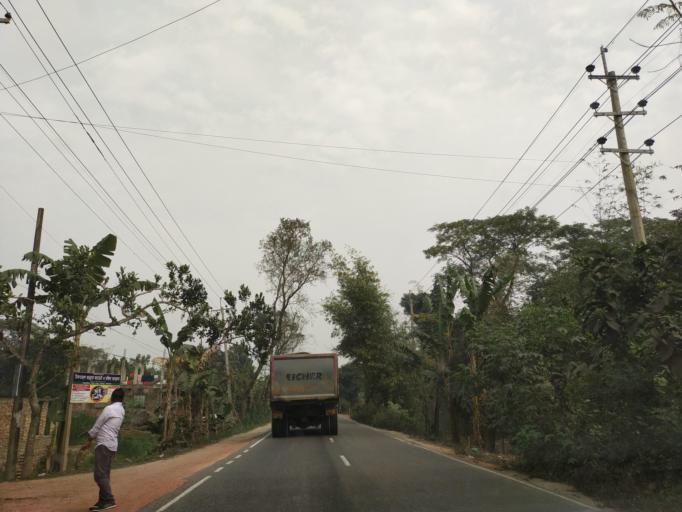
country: BD
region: Dhaka
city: Narsingdi
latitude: 24.0229
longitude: 90.7381
